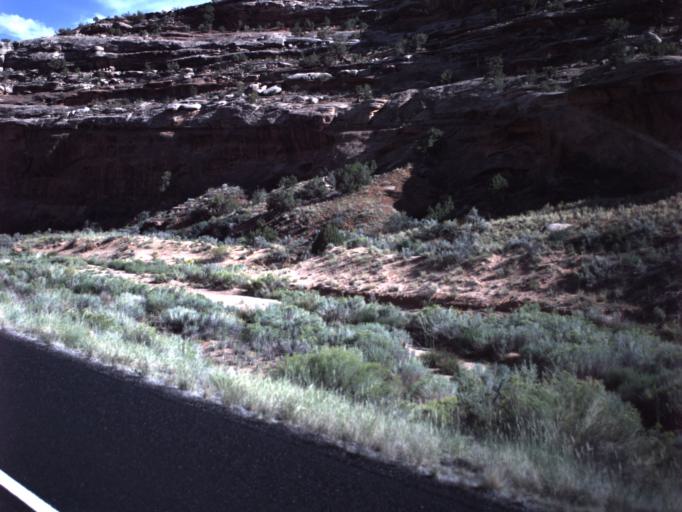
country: US
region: Utah
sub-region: Grand County
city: Moab
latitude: 38.6480
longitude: -109.7278
